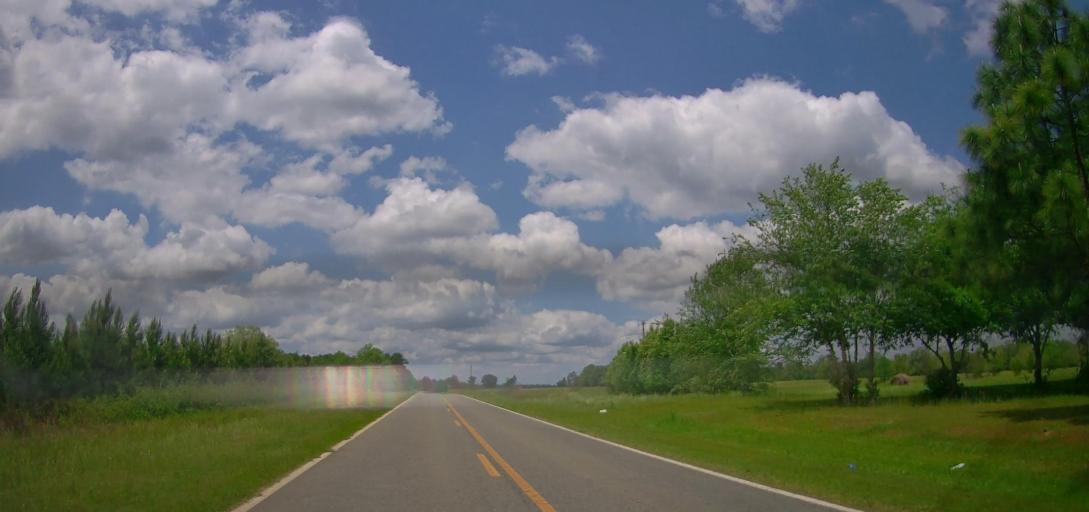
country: US
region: Georgia
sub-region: Laurens County
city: Dublin
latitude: 32.6028
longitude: -82.9853
